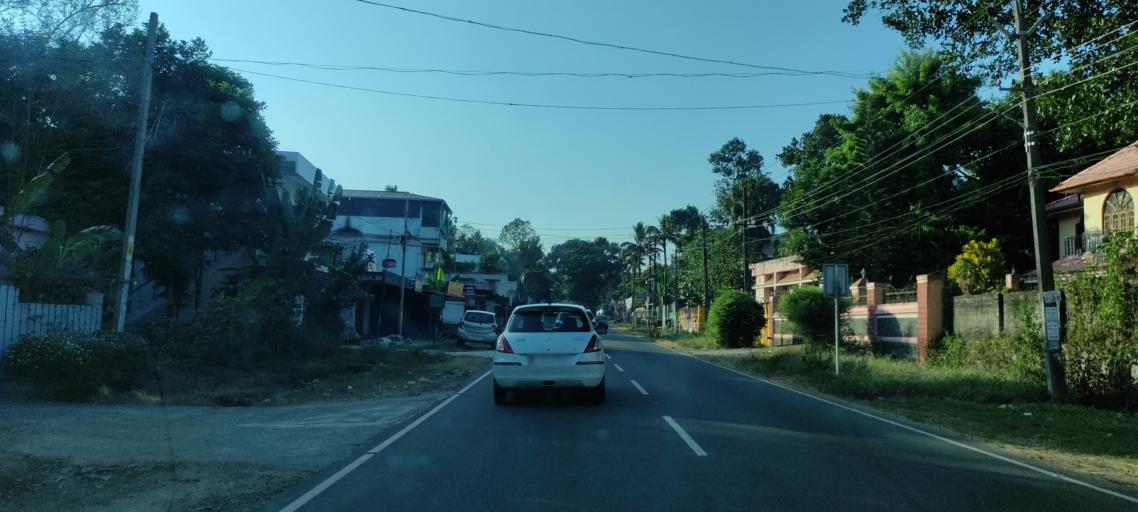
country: IN
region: Kerala
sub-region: Pattanamtitta
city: Adur
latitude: 9.1712
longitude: 76.6511
